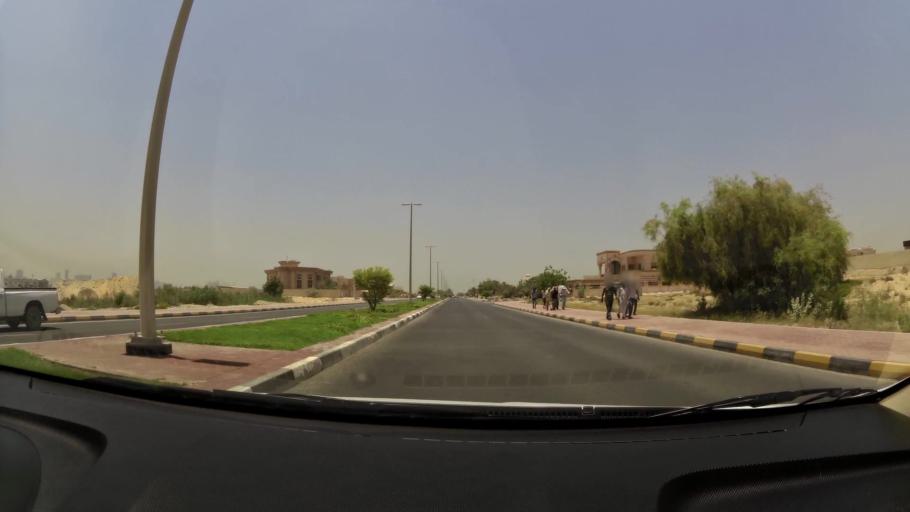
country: AE
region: Ajman
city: Ajman
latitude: 25.4071
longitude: 55.4882
